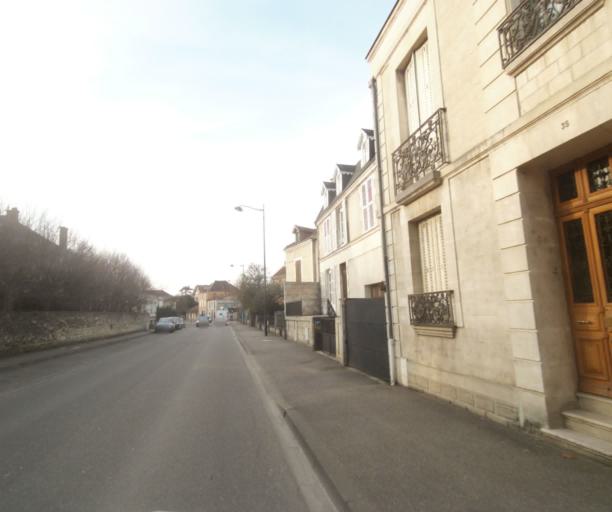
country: FR
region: Champagne-Ardenne
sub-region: Departement de la Haute-Marne
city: Saint-Dizier
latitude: 48.6397
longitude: 4.9445
